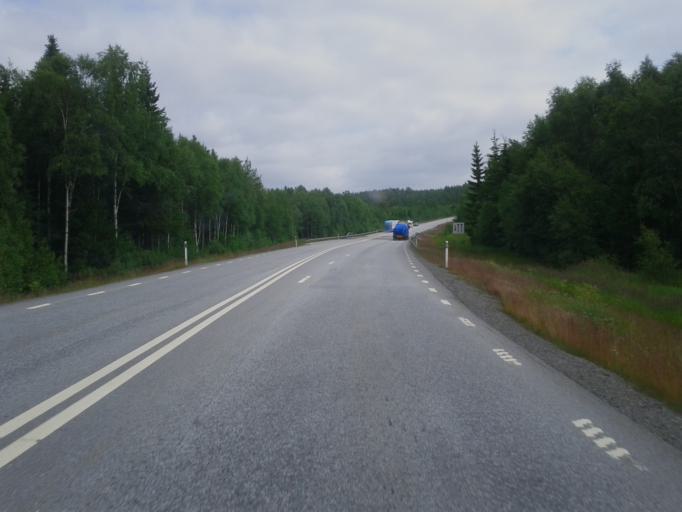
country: SE
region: Vaesterbotten
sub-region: Robertsfors Kommun
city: Robertsfors
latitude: 64.2923
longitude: 21.0807
